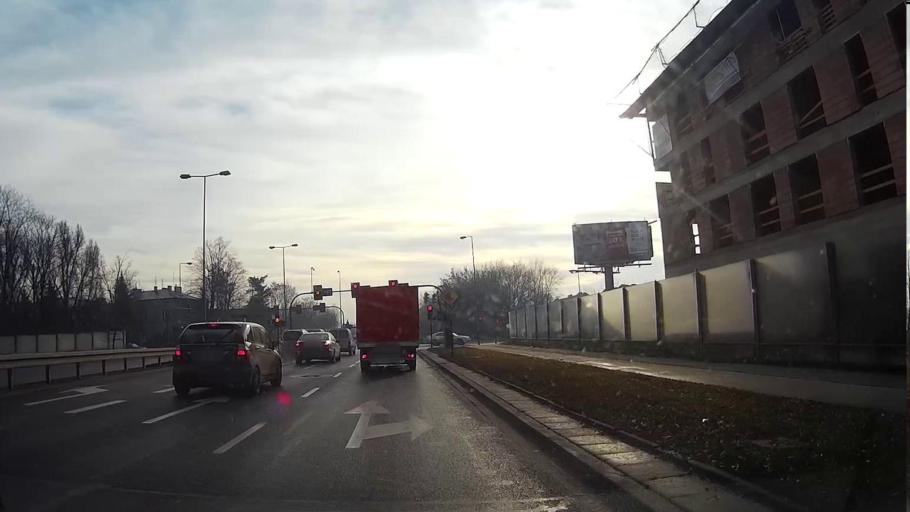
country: PL
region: Lesser Poland Voivodeship
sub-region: Krakow
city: Krakow
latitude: 50.0472
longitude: 19.9109
